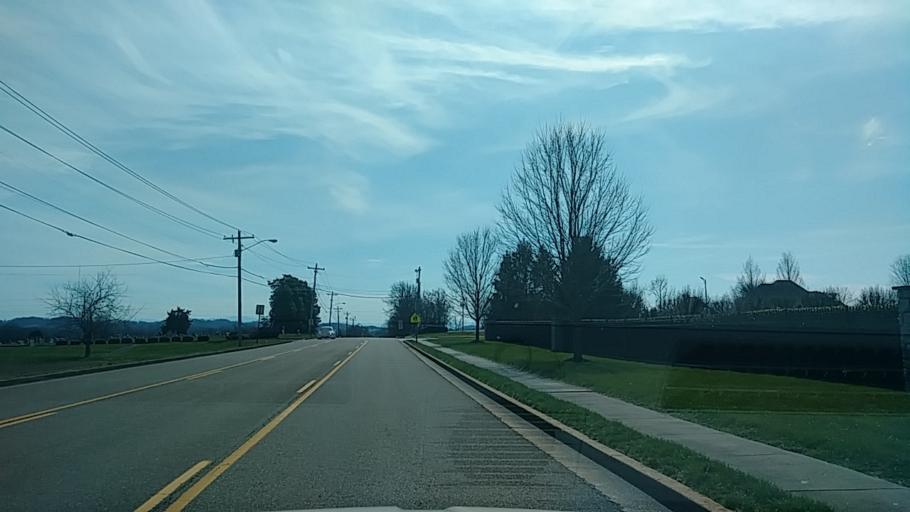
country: US
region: Tennessee
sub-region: Hamblen County
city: Morristown
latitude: 36.2110
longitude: -83.3344
